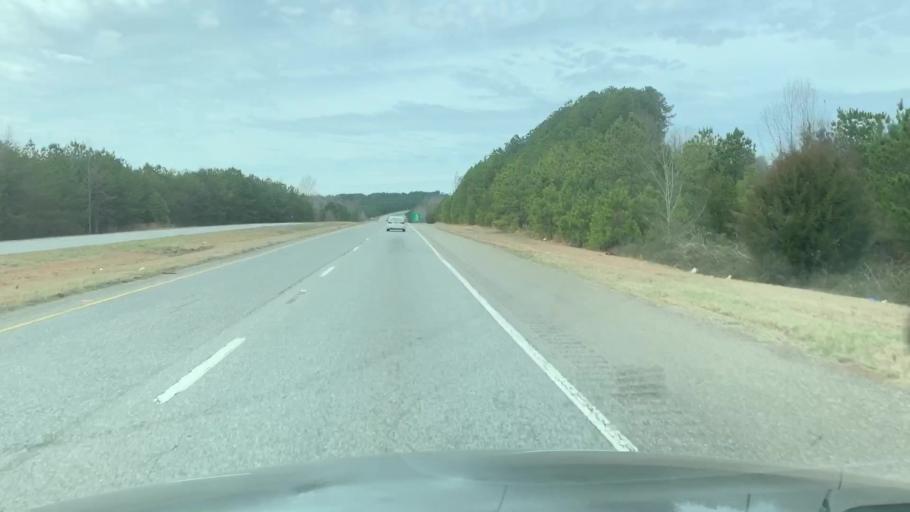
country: US
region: South Carolina
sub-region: Greenville County
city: Golden Grove
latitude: 34.7292
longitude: -82.4095
